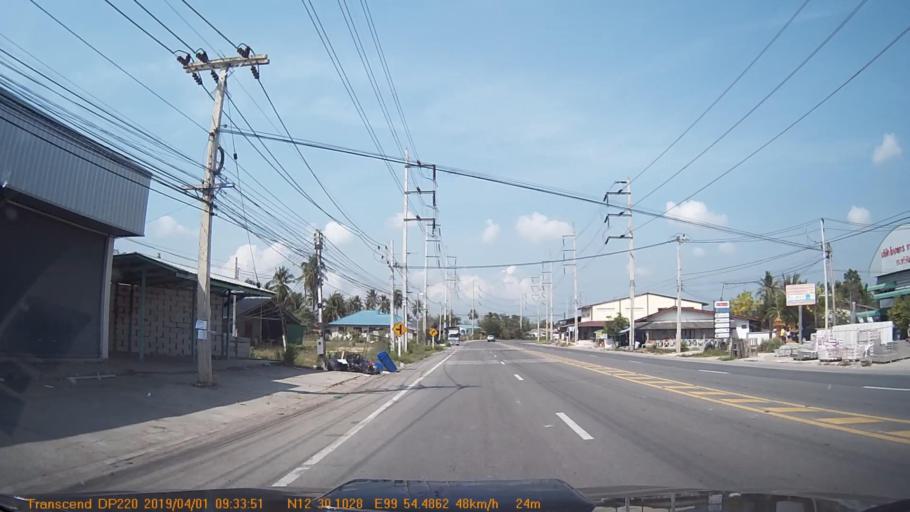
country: TH
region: Prachuap Khiri Khan
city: Hua Hin
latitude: 12.5016
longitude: 99.9080
